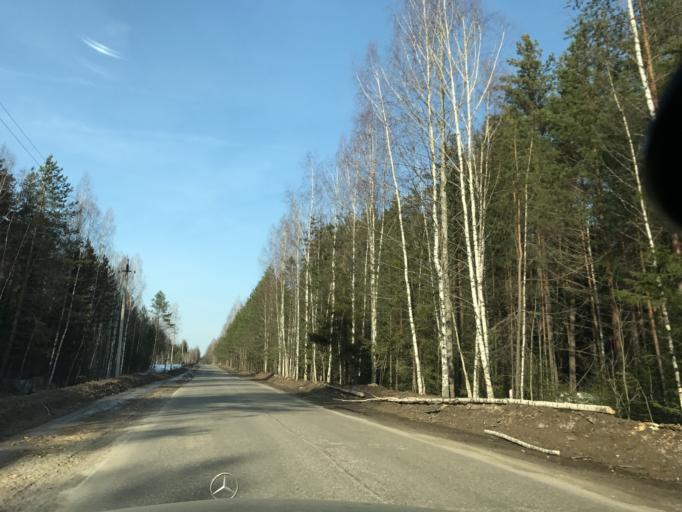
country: RU
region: Vladimir
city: Galitsy
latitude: 56.0143
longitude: 42.8592
